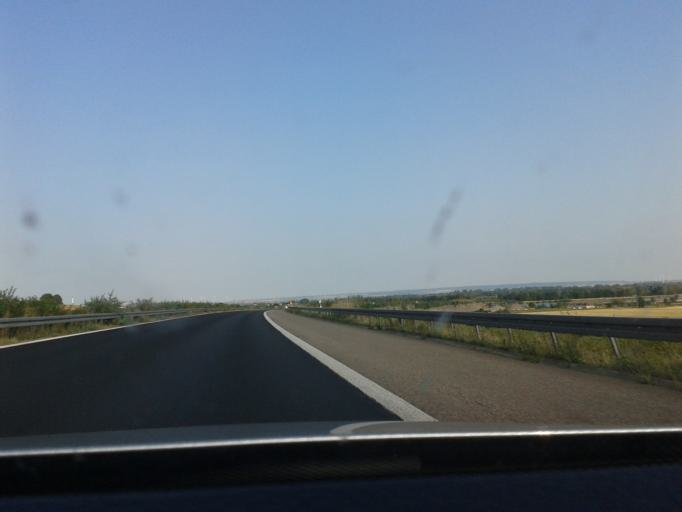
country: DE
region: Saxony-Anhalt
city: Wallhausen
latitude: 51.4626
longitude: 11.1774
